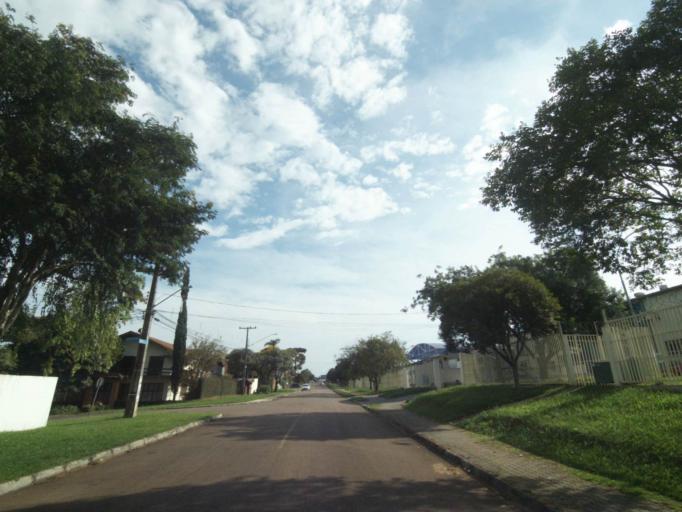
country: BR
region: Parana
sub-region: Pinhais
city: Pinhais
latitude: -25.4409
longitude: -49.2228
